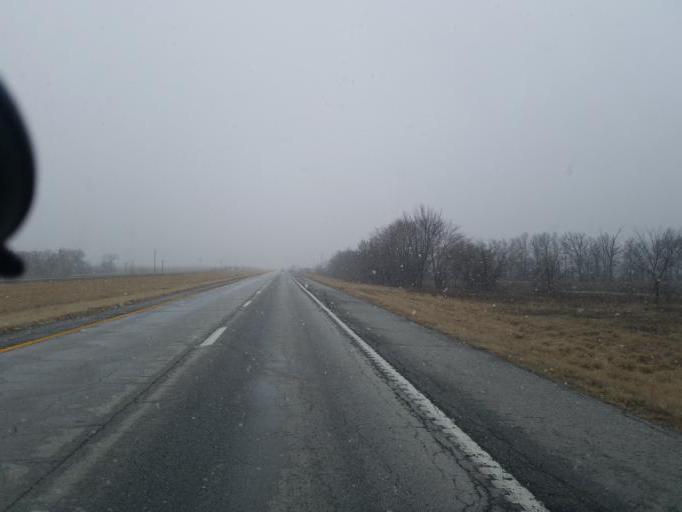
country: US
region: Missouri
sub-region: Macon County
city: La Plata
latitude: 39.9655
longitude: -92.4765
